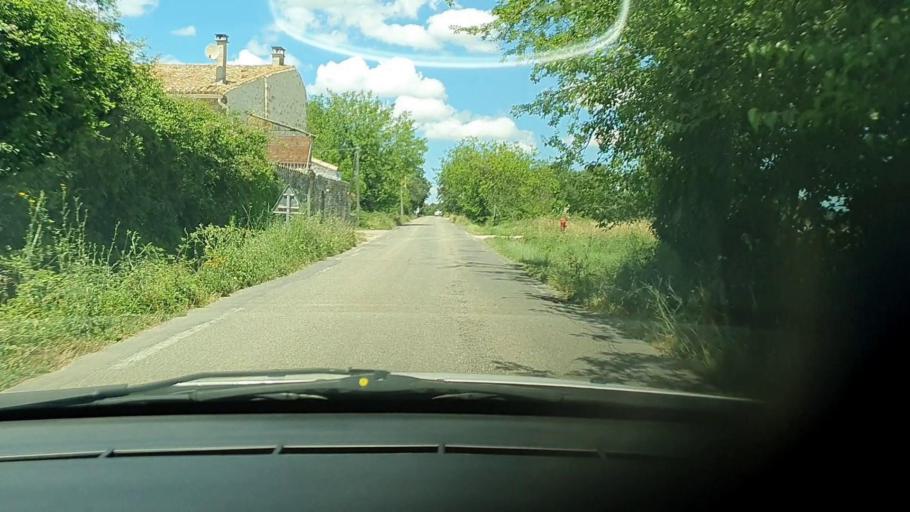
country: FR
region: Languedoc-Roussillon
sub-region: Departement du Gard
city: Blauzac
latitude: 43.9767
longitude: 4.3709
